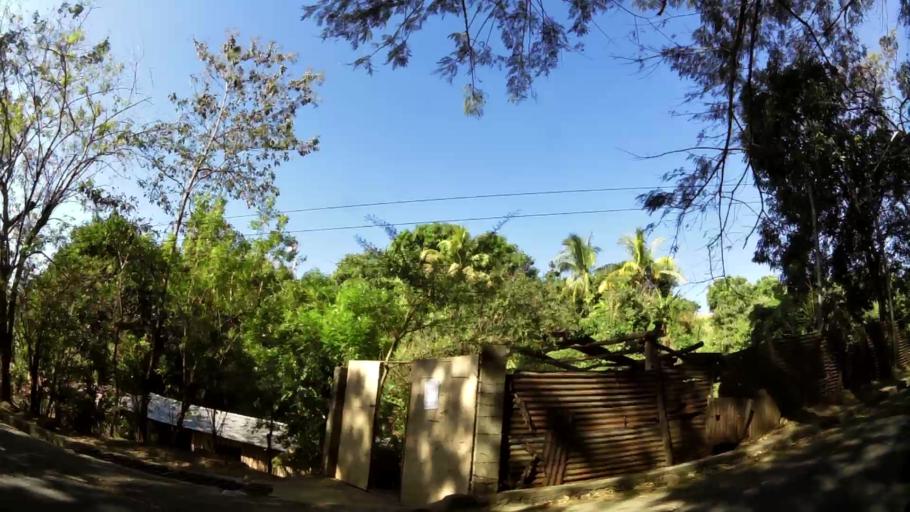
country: SV
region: Sonsonate
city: Sonzacate
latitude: 13.7385
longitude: -89.7343
